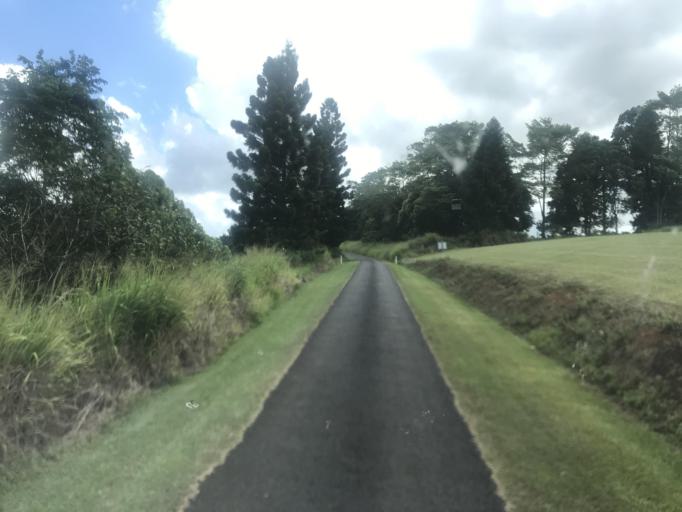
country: AU
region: Queensland
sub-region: Tablelands
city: Ravenshoe
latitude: -17.5523
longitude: 145.6957
